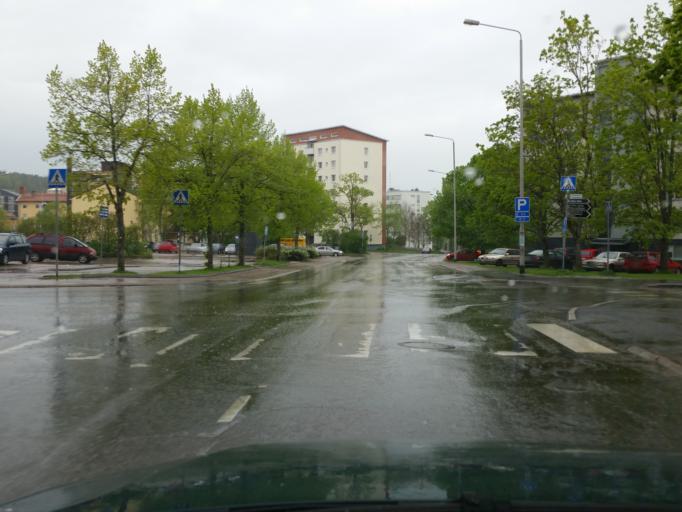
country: FI
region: Uusimaa
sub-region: Helsinki
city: Lohja
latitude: 60.2520
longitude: 24.0636
